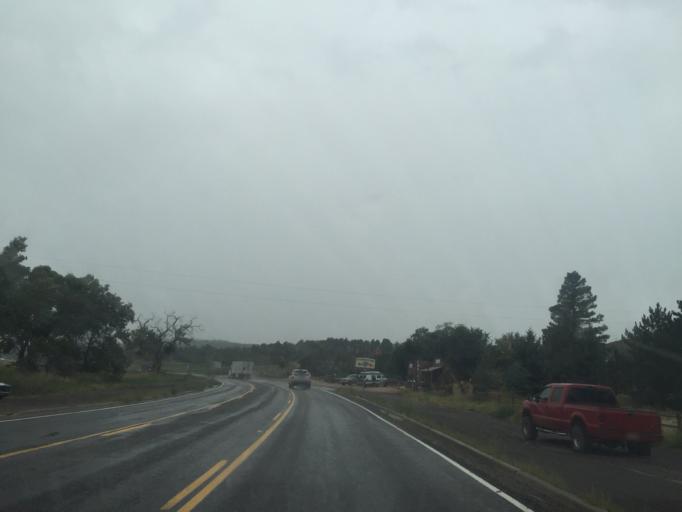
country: US
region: Utah
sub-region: Kane County
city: Kanab
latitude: 37.2722
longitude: -112.6483
